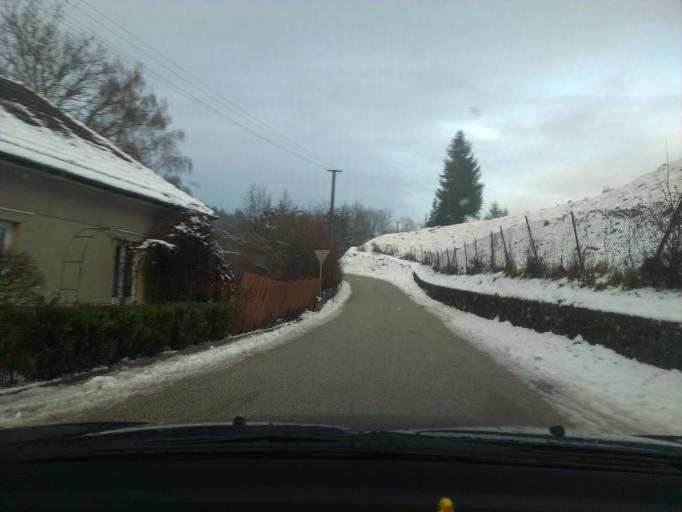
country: SK
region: Trnavsky
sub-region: Okres Trnava
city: Piestany
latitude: 48.6496
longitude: 17.9415
